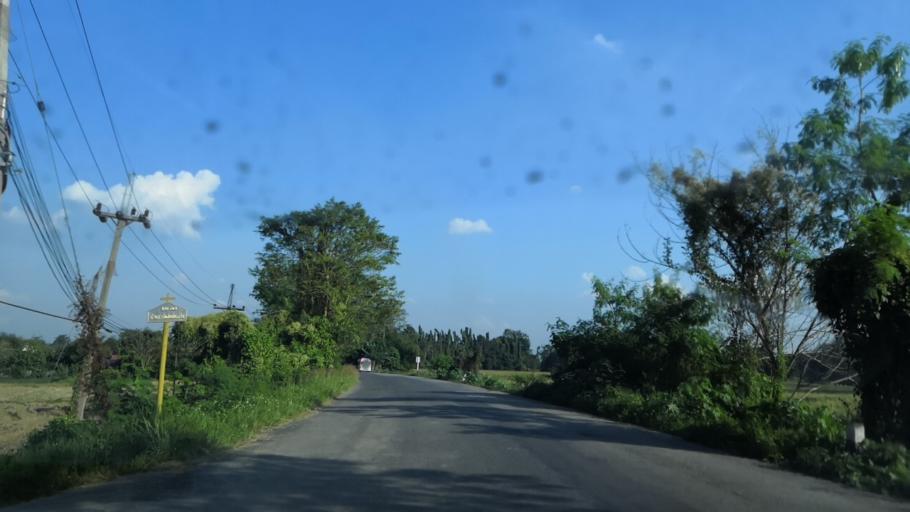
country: TH
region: Chiang Rai
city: Wiang Chai
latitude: 19.9476
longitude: 99.9239
